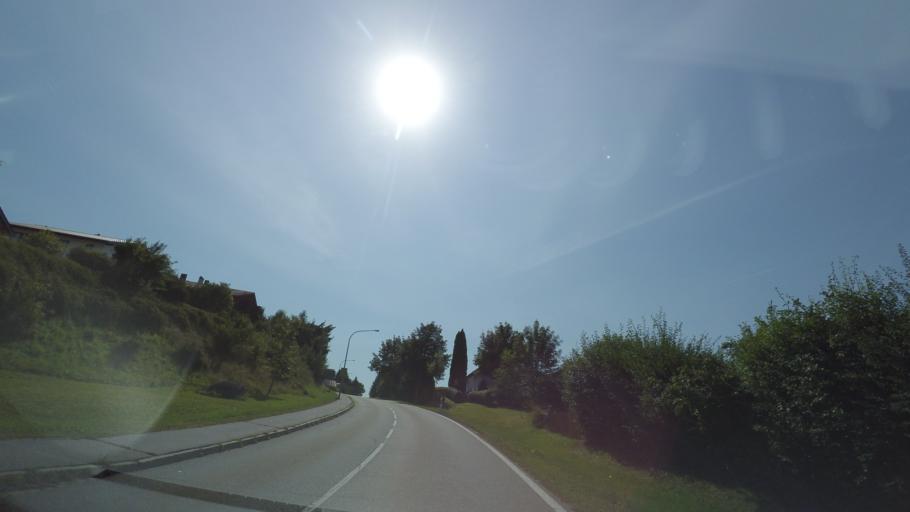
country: DE
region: Bavaria
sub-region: Lower Bavaria
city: Geiersthal
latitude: 49.0476
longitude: 12.9768
